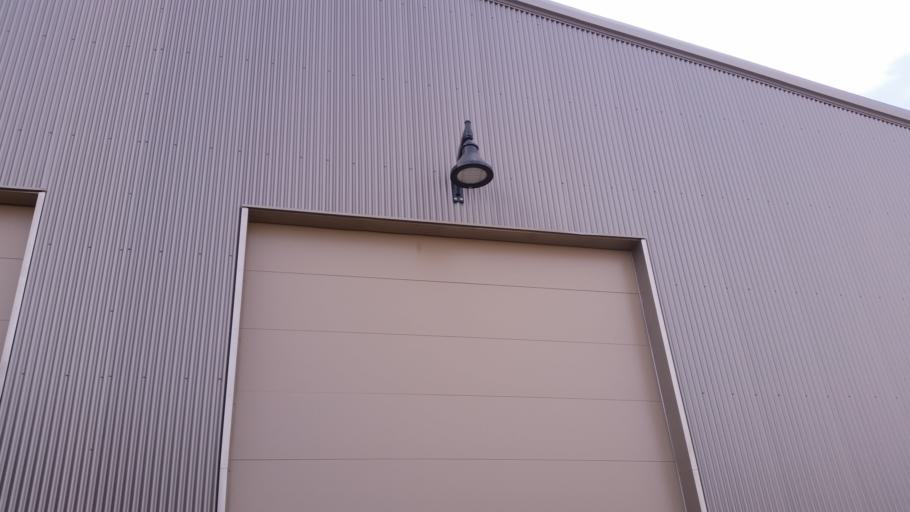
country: US
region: Washington
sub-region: Lincoln County
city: Davenport
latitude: 47.6640
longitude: -117.9374
